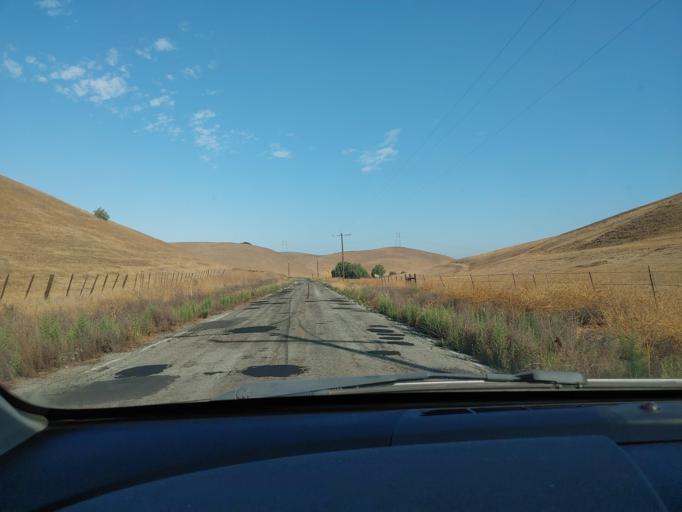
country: US
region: California
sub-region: San Benito County
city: Ridgemark
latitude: 36.8035
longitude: -121.2963
